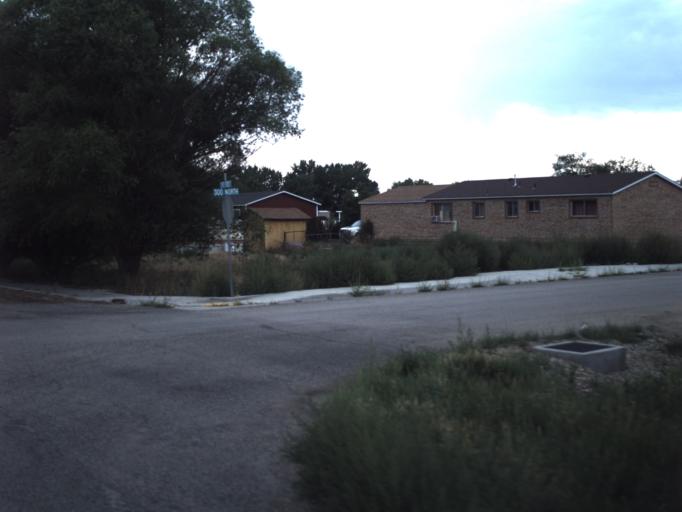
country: US
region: Utah
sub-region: Emery County
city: Huntington
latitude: 39.3531
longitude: -110.8520
